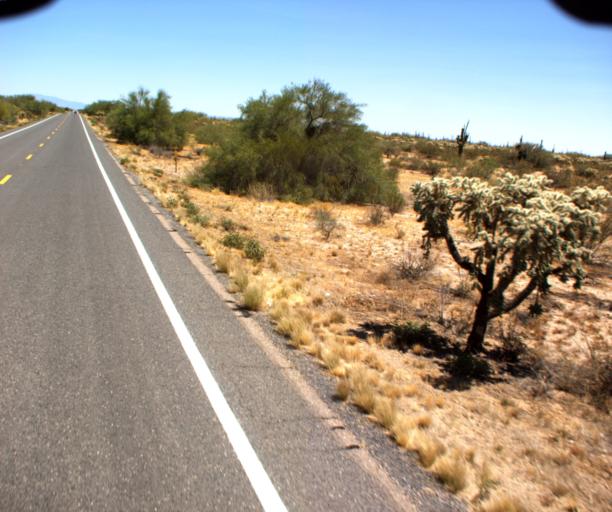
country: US
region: Arizona
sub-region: Pinal County
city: Florence
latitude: 32.8691
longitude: -111.2485
